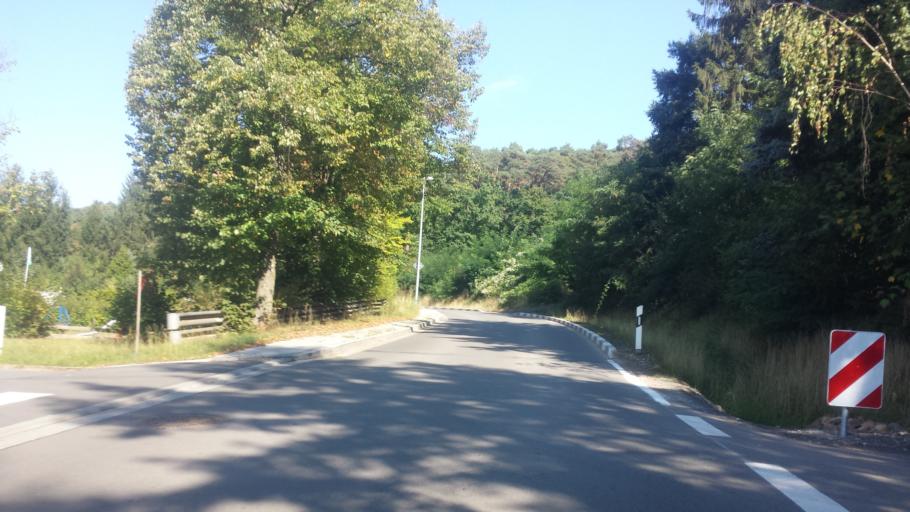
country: DE
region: Rheinland-Pfalz
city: Eisenberg
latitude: 49.5496
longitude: 8.0480
